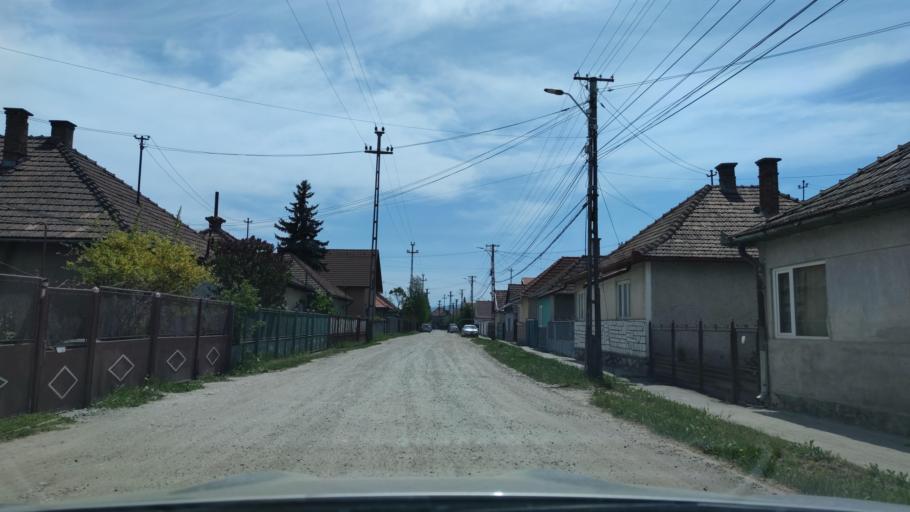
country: RO
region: Harghita
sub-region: Municipiul Gheorgheni
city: Gheorgheni
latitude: 46.7189
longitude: 25.5824
